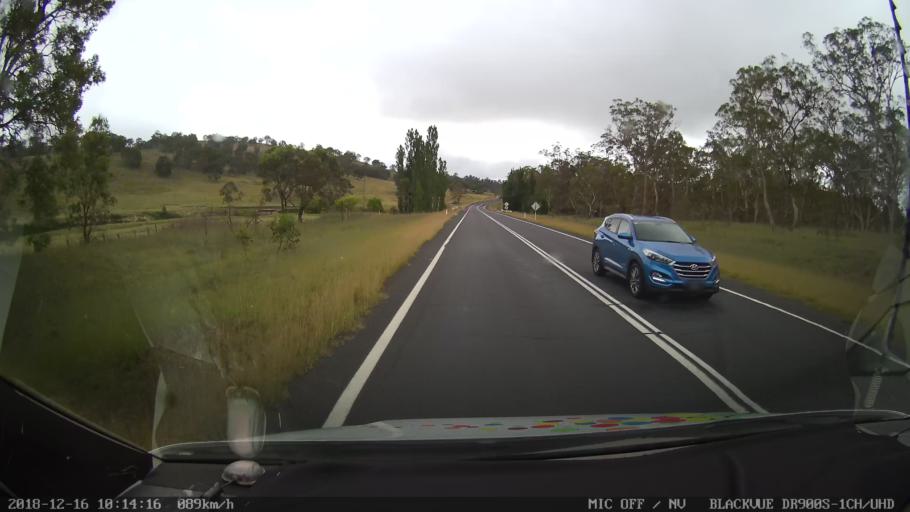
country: AU
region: New South Wales
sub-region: Tenterfield Municipality
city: Carrolls Creek
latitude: -29.2888
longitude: 151.9615
